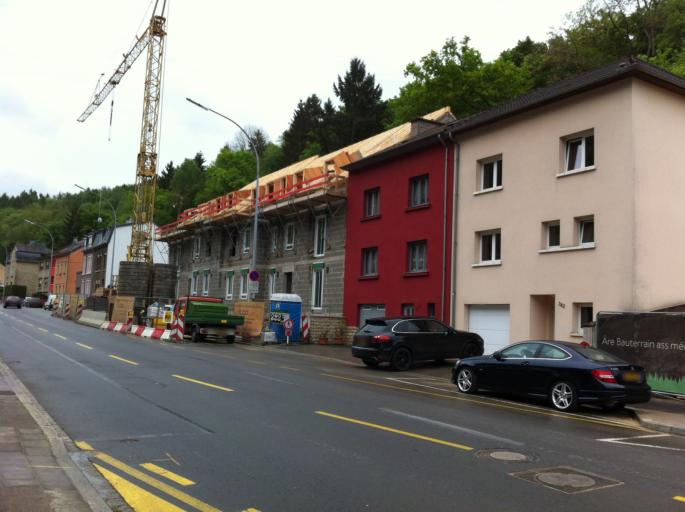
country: LU
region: Luxembourg
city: Kirchberg
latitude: 49.6242
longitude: 6.1730
